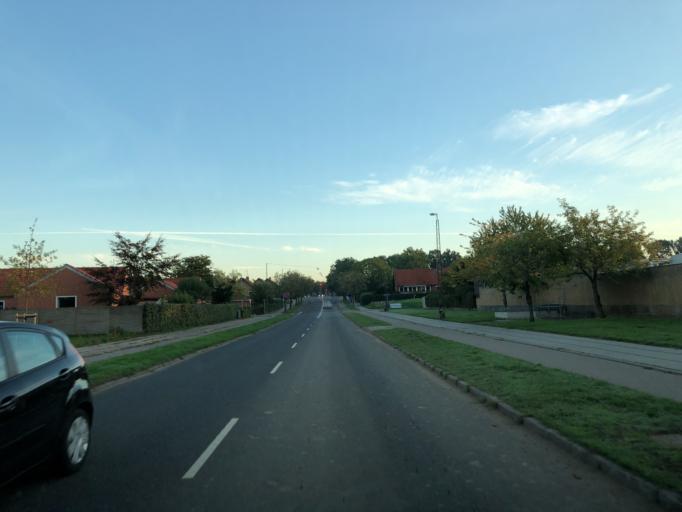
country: DK
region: South Denmark
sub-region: Sonderborg Kommune
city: Sonderborg
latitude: 54.9014
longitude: 9.8097
